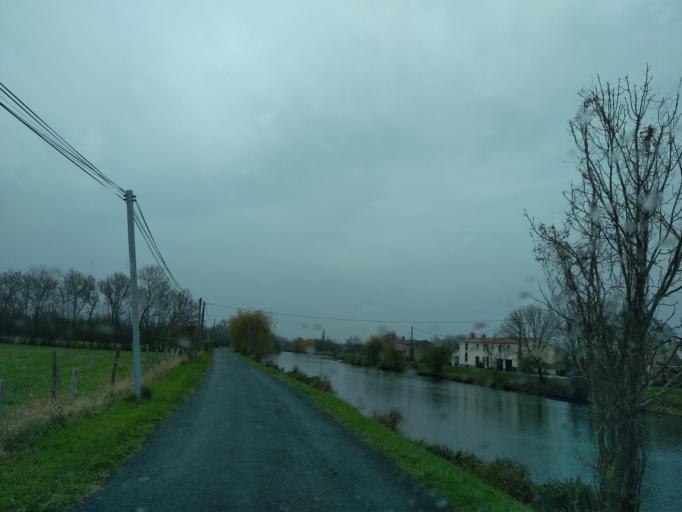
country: FR
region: Pays de la Loire
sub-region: Departement de la Vendee
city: Maillezais
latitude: 46.3193
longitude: -0.7844
